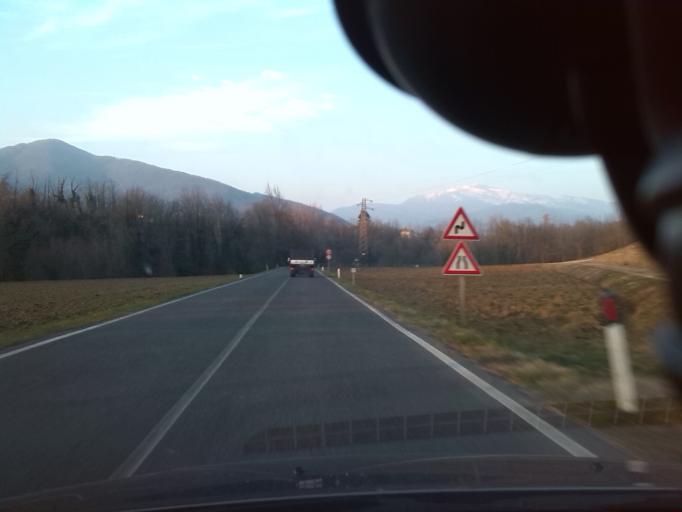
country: IT
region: Friuli Venezia Giulia
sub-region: Provincia di Udine
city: San Pietro al Natisone
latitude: 46.1077
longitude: 13.4743
